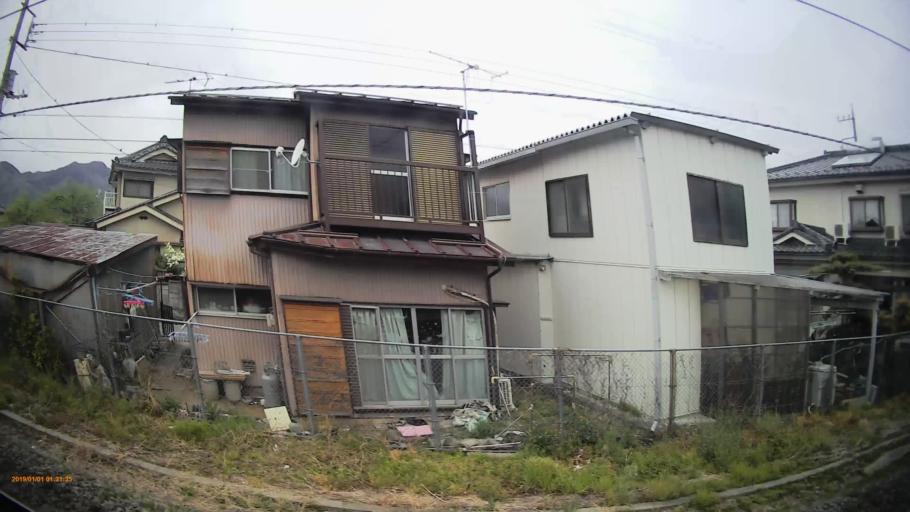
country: JP
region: Yamanashi
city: Enzan
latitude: 35.6915
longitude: 138.6979
